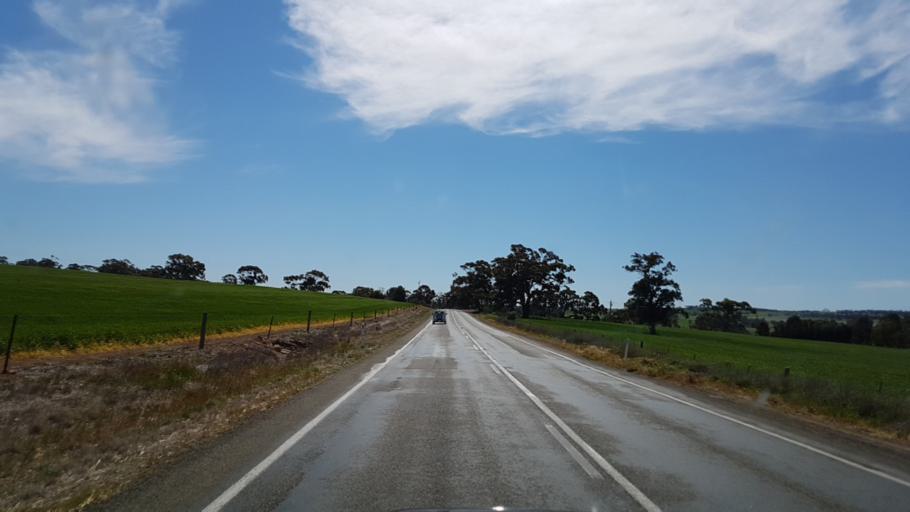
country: AU
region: South Australia
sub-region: Clare and Gilbert Valleys
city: Clare
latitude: -34.0146
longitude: 138.8112
